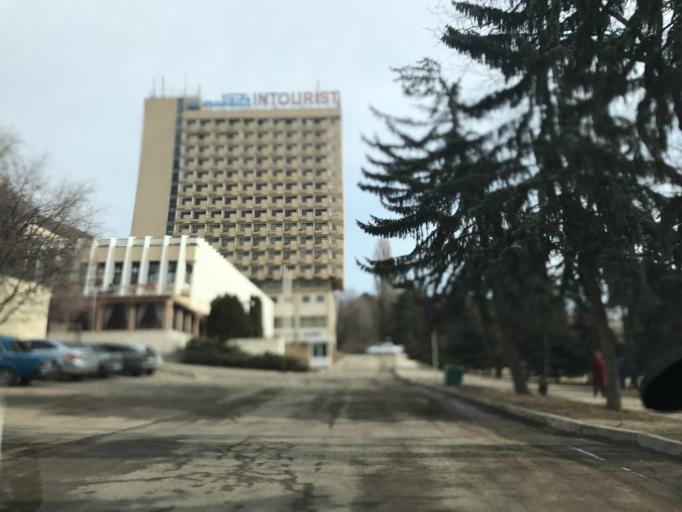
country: RU
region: Stavropol'skiy
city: Pyatigorsk
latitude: 44.0404
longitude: 43.0724
